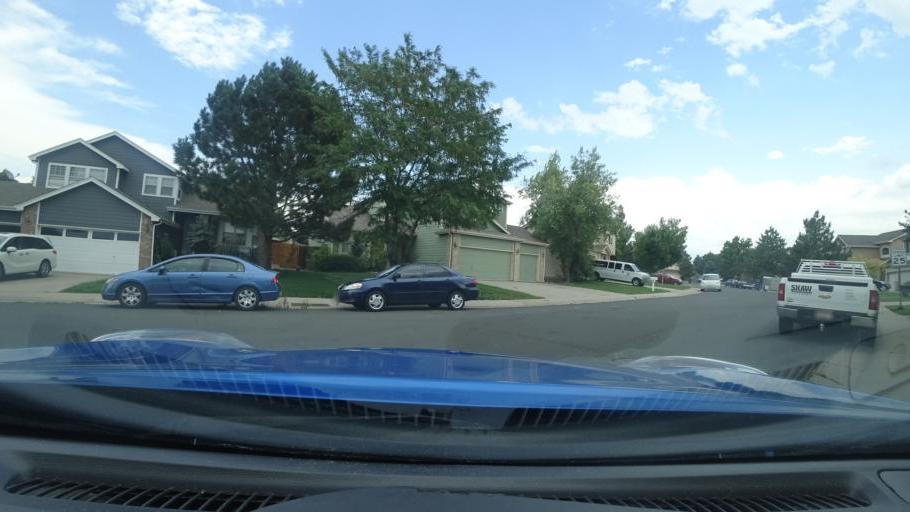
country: US
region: Colorado
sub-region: Adams County
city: Aurora
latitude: 39.6903
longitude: -104.7904
